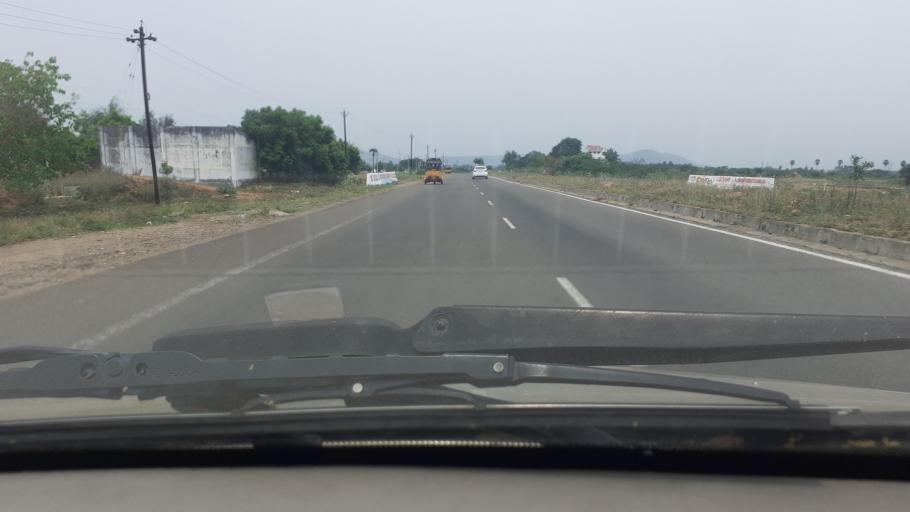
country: IN
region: Tamil Nadu
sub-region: Tirunelveli Kattabo
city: Tirunelveli
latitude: 8.7118
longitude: 77.8025
